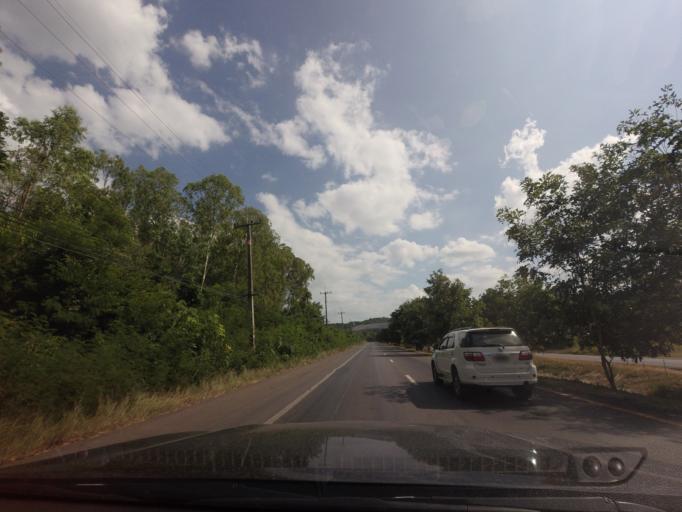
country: TH
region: Phetchabun
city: Wichian Buri
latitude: 15.6342
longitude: 101.0468
